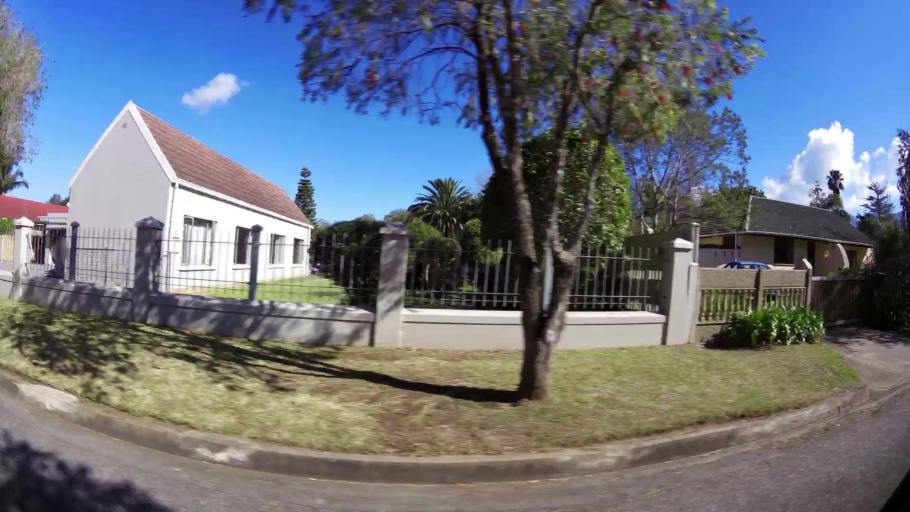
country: ZA
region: Western Cape
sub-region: Eden District Municipality
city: George
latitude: -33.9546
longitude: 22.4293
